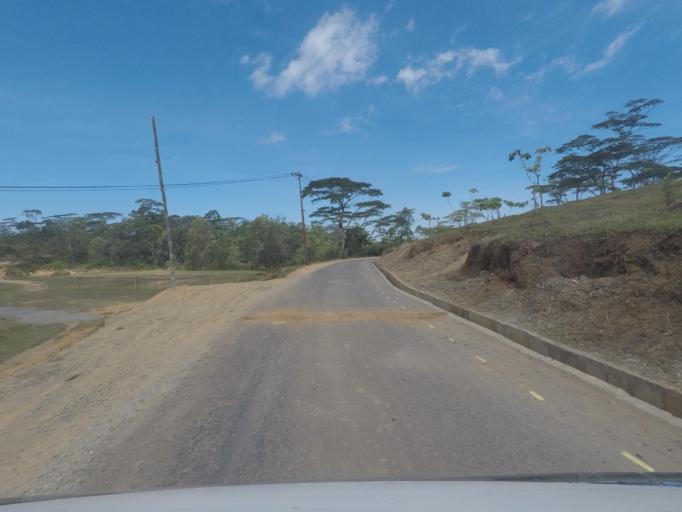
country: TL
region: Ermera
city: Gleno
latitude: -8.7474
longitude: 125.3436
